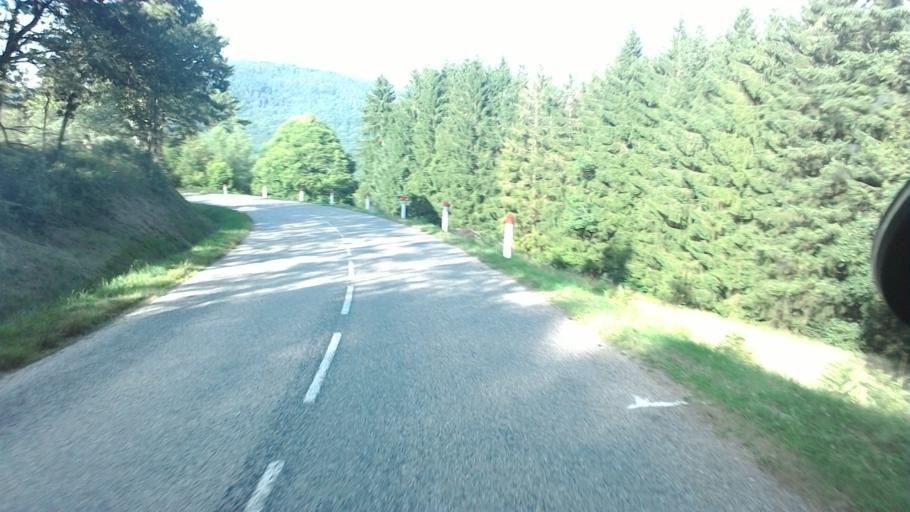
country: FR
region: Lorraine
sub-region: Departement des Vosges
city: Rupt-sur-Moselle
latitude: 47.9098
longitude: 6.6469
